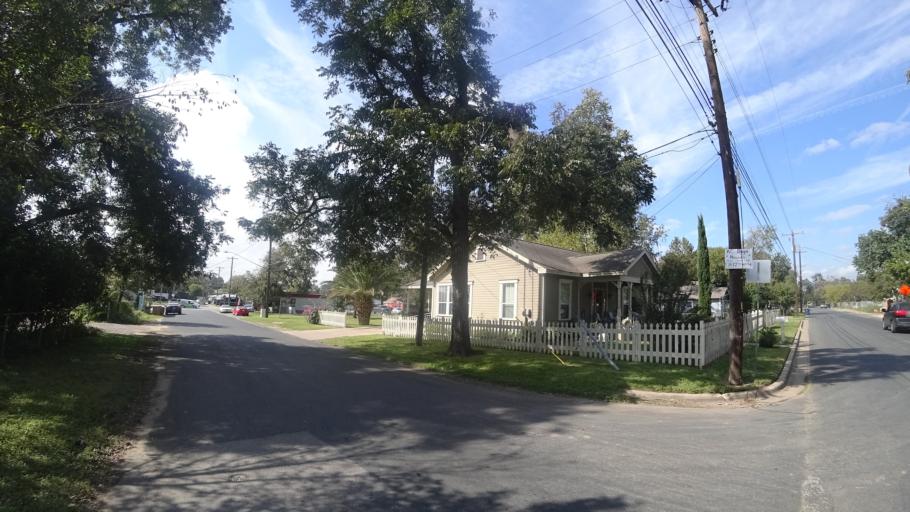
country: US
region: Texas
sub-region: Travis County
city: Austin
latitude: 30.2578
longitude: -97.7026
